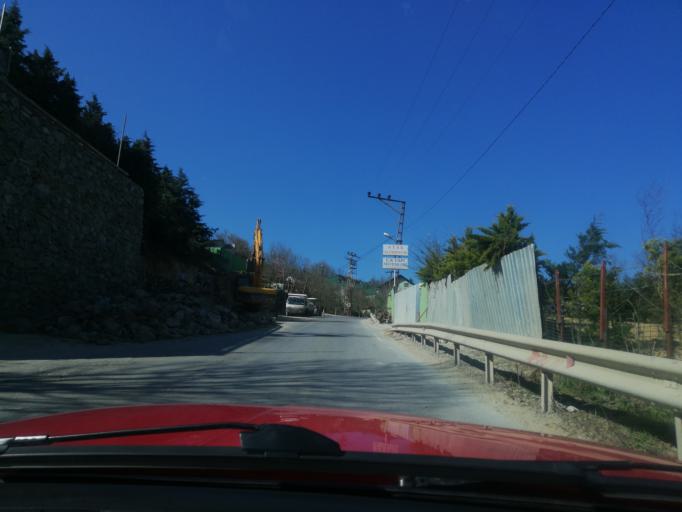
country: TR
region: Istanbul
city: Mahmut Sevket Pasa
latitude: 41.1024
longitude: 29.1587
